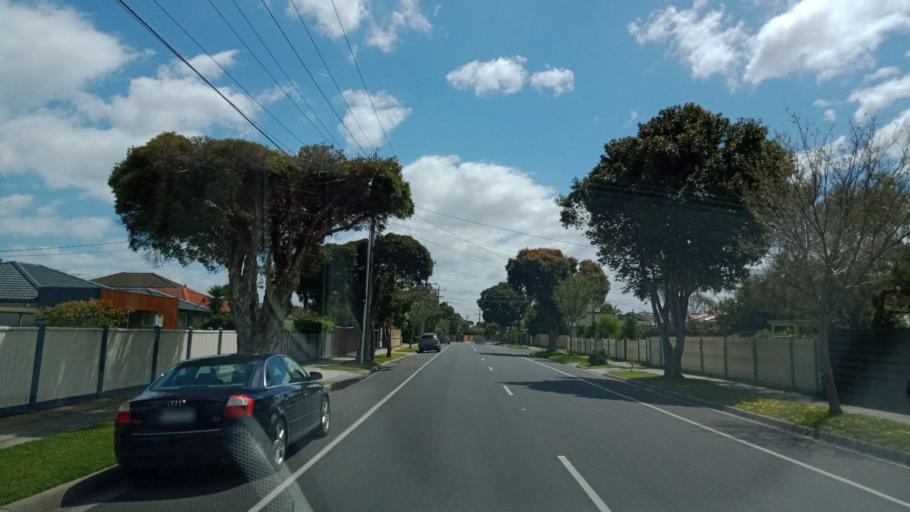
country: AU
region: Victoria
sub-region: Kingston
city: Chelsea Heights
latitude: -38.0486
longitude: 145.1362
